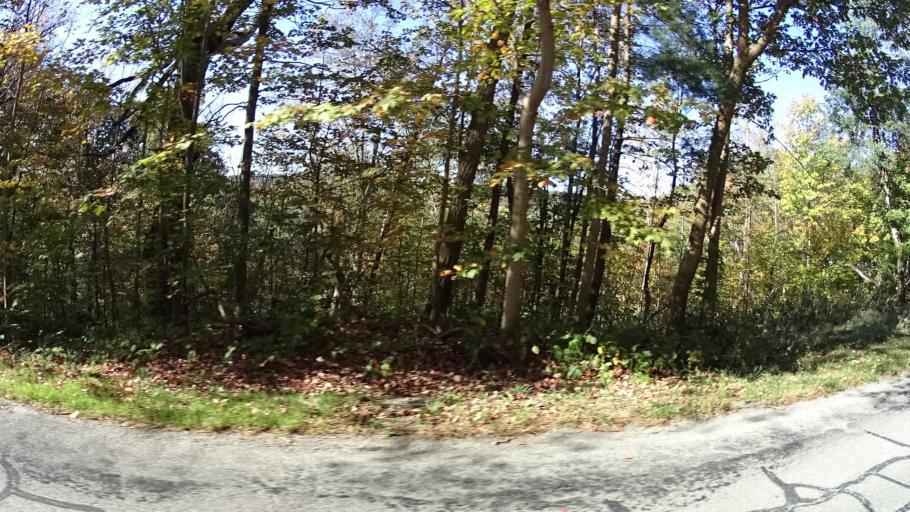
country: US
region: Ohio
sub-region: Lorain County
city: Vermilion-on-the-Lake
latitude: 41.3884
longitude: -82.3191
